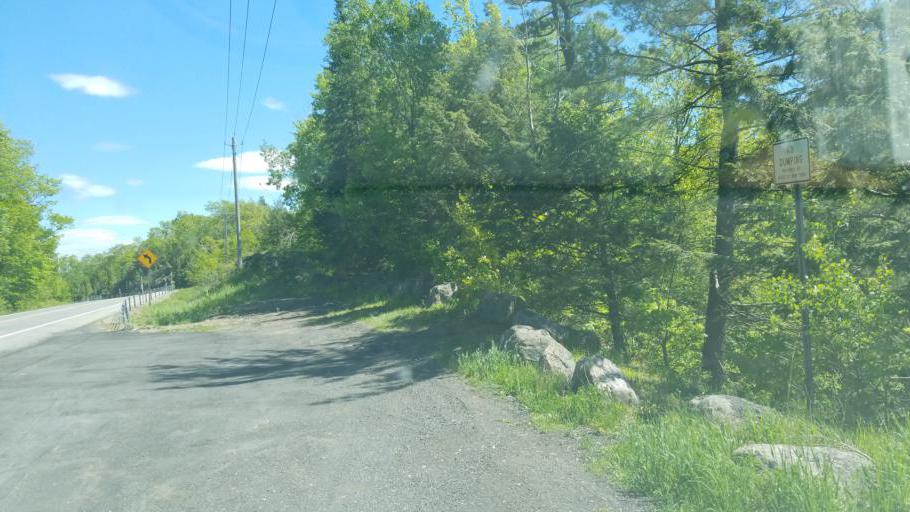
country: US
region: New York
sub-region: Fulton County
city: Gloversville
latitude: 43.1671
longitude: -74.5009
